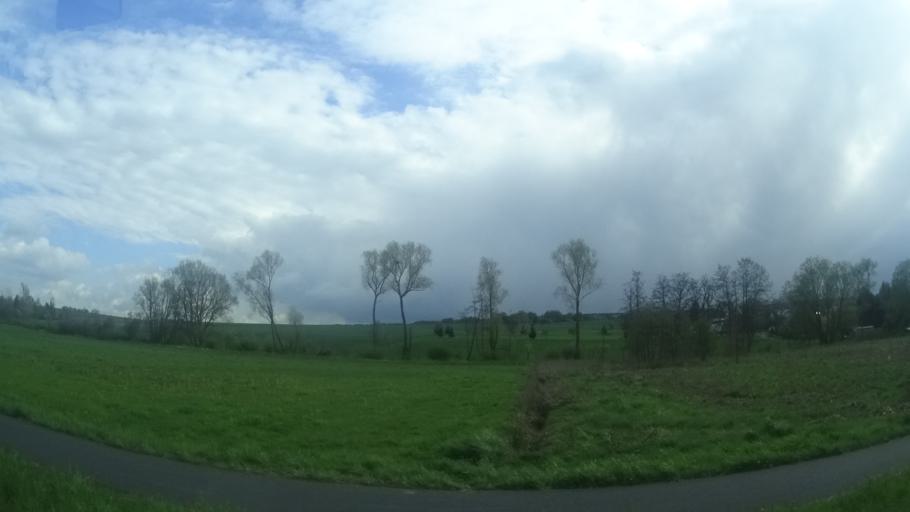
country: DE
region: Hesse
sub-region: Regierungsbezirk Giessen
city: Hoernsheim
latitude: 50.5179
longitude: 8.5895
